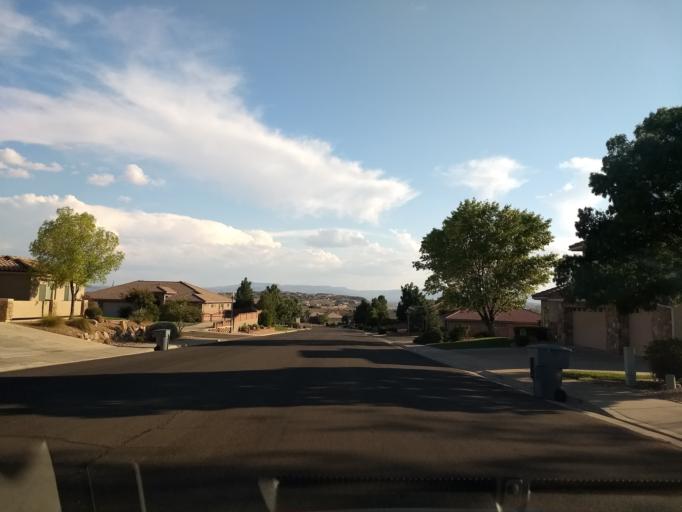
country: US
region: Utah
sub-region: Washington County
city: Saint George
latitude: 37.0996
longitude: -113.5459
